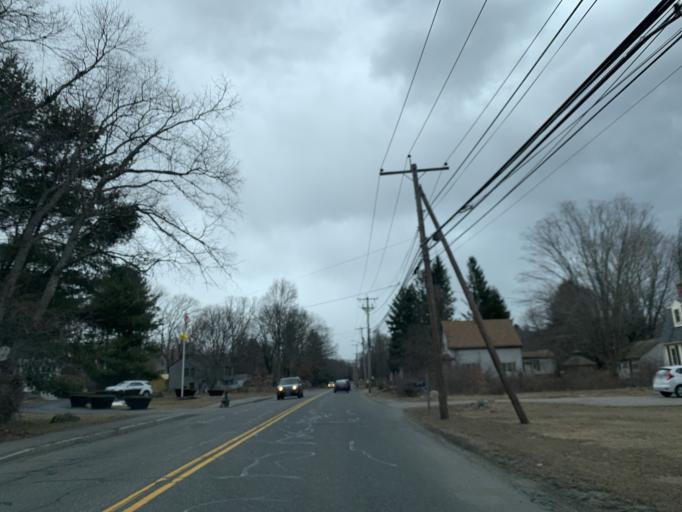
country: US
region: Massachusetts
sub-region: Norfolk County
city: Franklin
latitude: 42.0880
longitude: -71.3813
